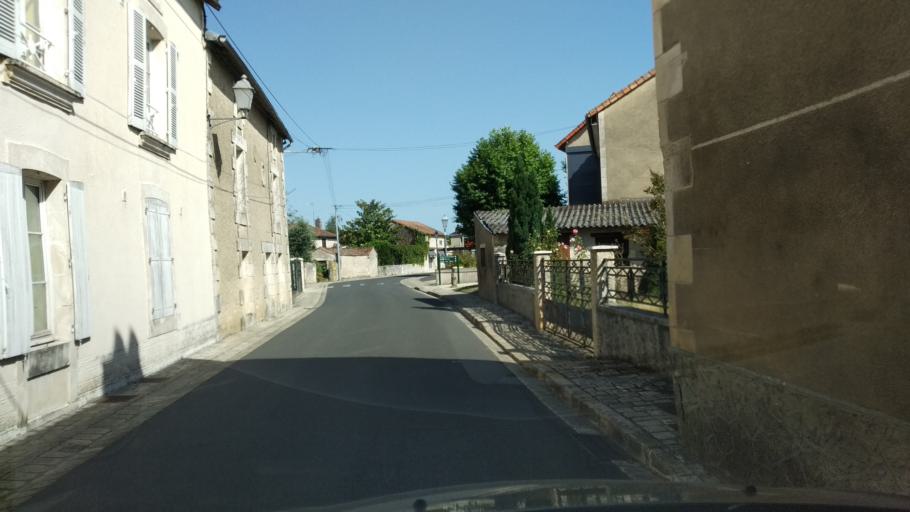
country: FR
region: Poitou-Charentes
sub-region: Departement de la Vienne
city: Lussac-les-Chateaux
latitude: 46.4447
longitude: 0.6652
